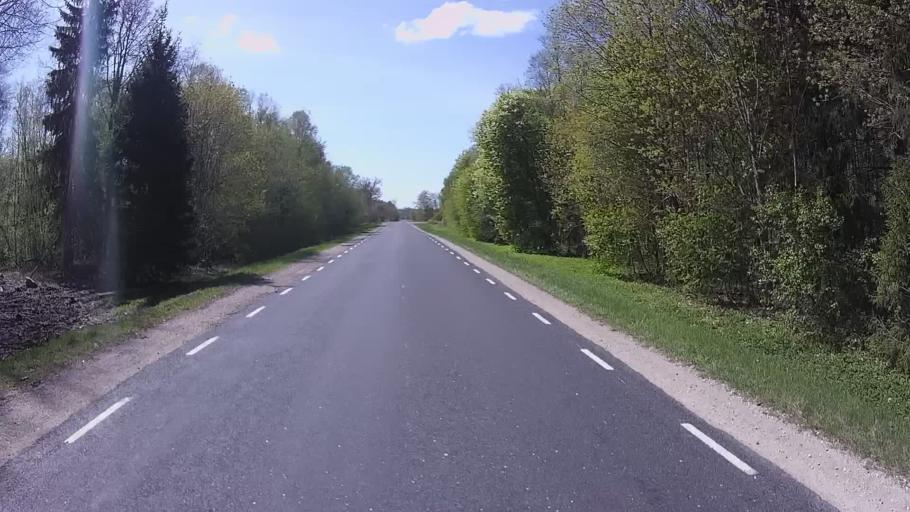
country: EE
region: Laeaene
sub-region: Ridala Parish
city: Uuemoisa
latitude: 59.0175
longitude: 23.7947
